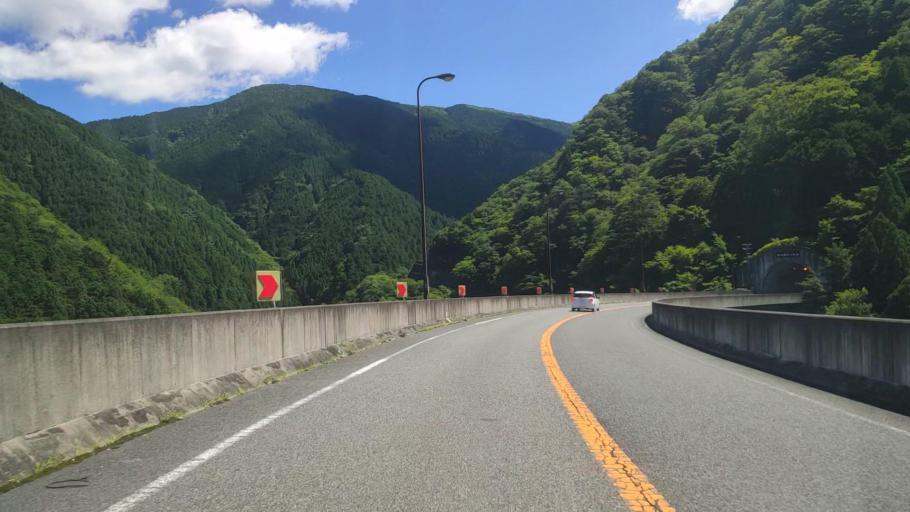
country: JP
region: Nara
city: Yoshino-cho
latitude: 34.2498
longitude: 135.9996
